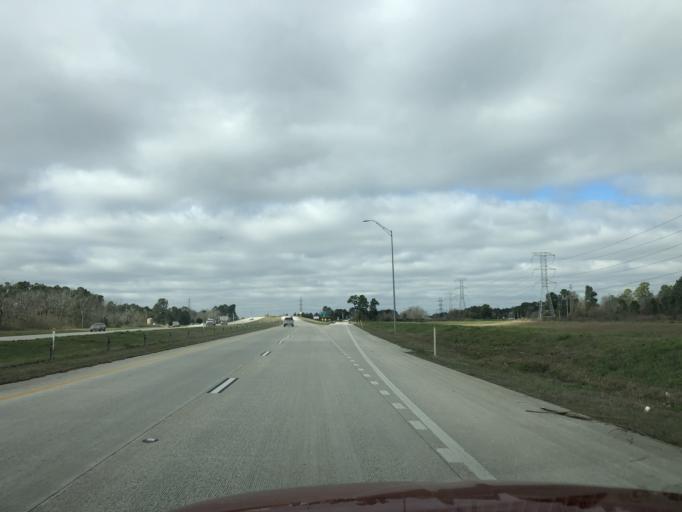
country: US
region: Texas
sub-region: Montgomery County
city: The Woodlands
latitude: 30.0945
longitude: -95.5005
